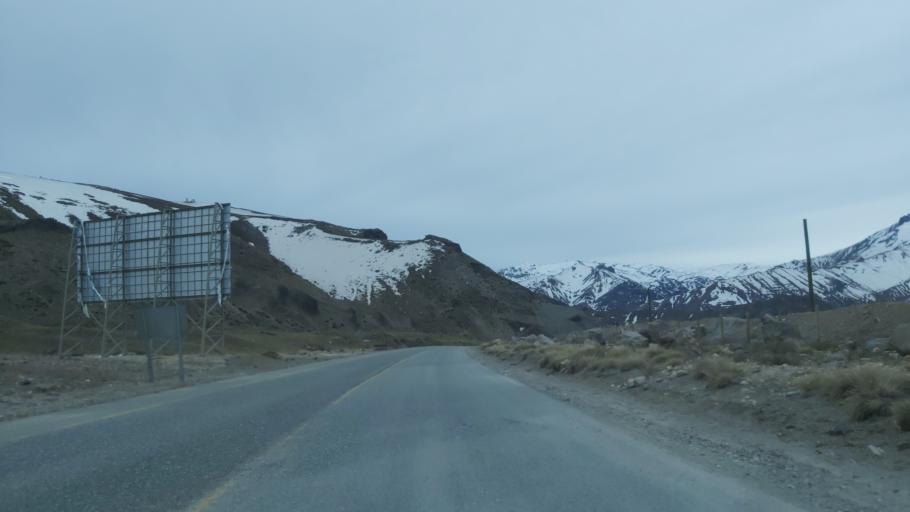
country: CL
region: Maule
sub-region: Provincia de Linares
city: Colbun
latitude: -35.9677
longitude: -70.5704
